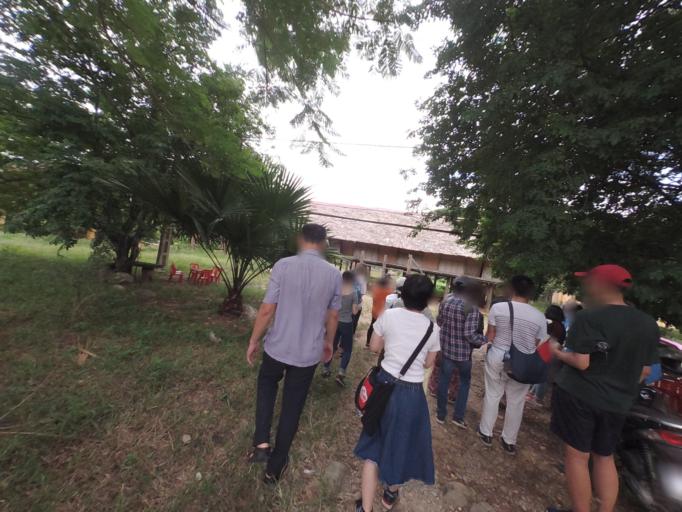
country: VN
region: Thua Thien-Hue
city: A Luoi
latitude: 16.3012
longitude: 107.3365
